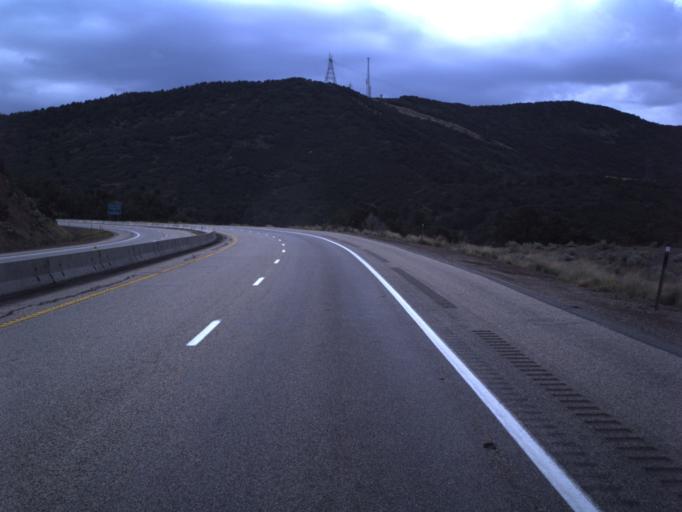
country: US
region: Utah
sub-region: Beaver County
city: Beaver
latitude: 38.5990
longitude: -112.5080
